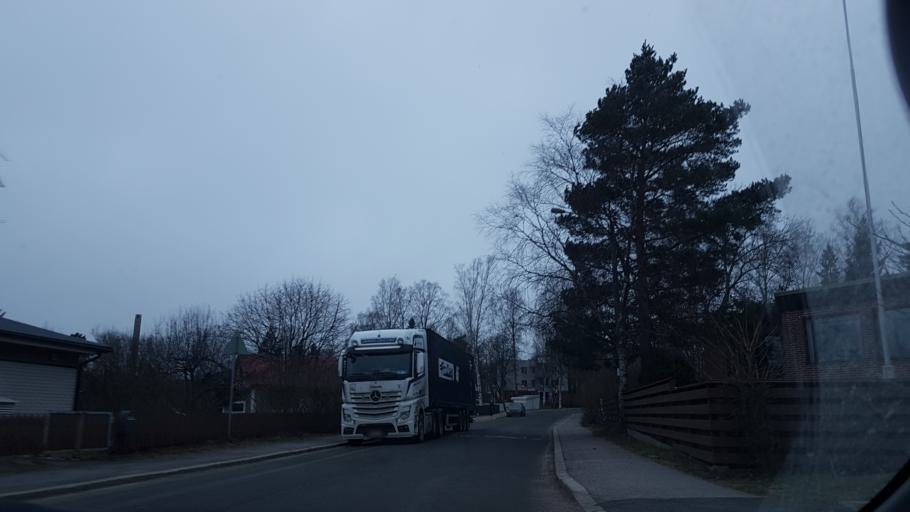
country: FI
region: Uusimaa
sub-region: Helsinki
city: Vantaa
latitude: 60.2287
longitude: 25.0944
